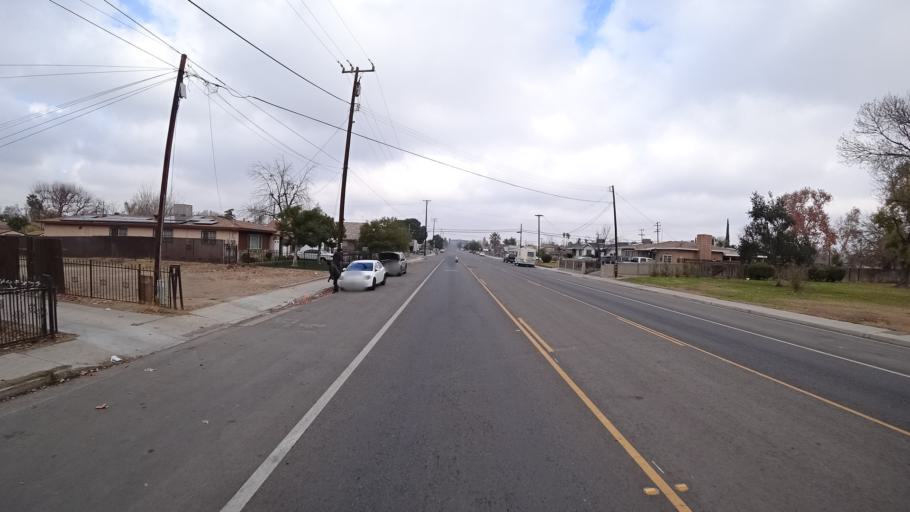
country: US
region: California
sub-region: Kern County
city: Bakersfield
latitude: 35.3618
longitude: -119.0119
